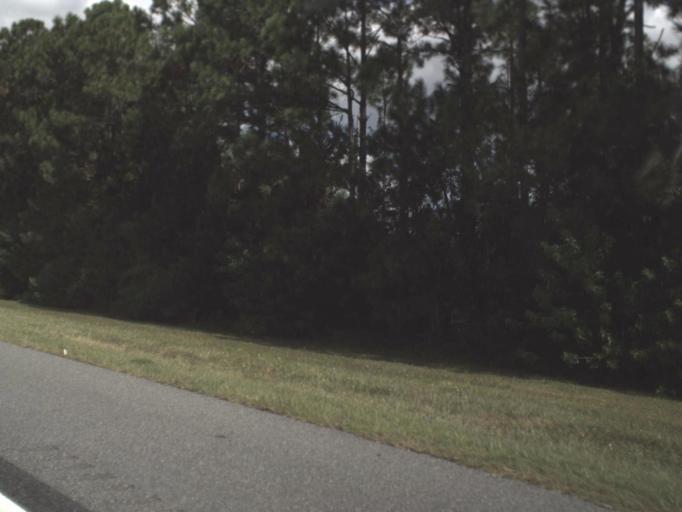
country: US
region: Florida
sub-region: Orange County
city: Southchase
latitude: 28.4150
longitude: -81.3915
